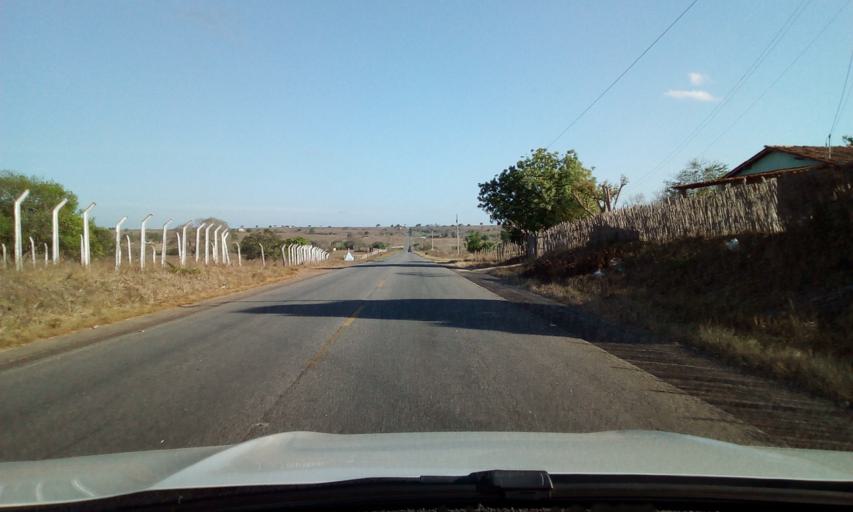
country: BR
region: Paraiba
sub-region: Mulungu
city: Mulungu
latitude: -6.9655
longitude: -35.4077
